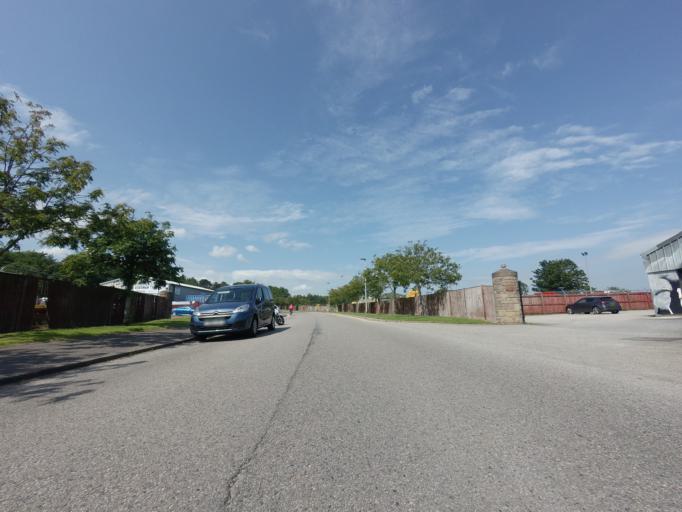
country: GB
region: Scotland
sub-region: Highland
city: Tain
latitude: 57.8171
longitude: -4.0603
